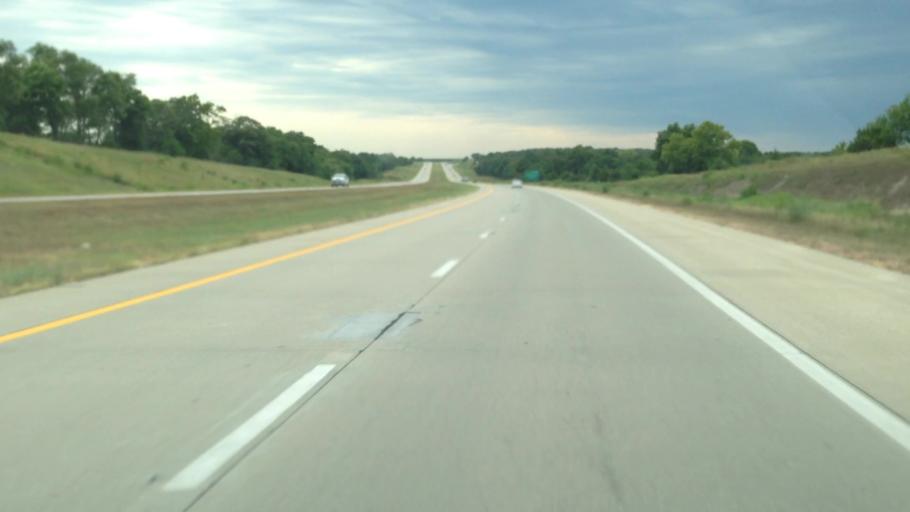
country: US
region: Kansas
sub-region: Franklin County
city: Ottawa
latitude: 38.5494
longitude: -95.3614
